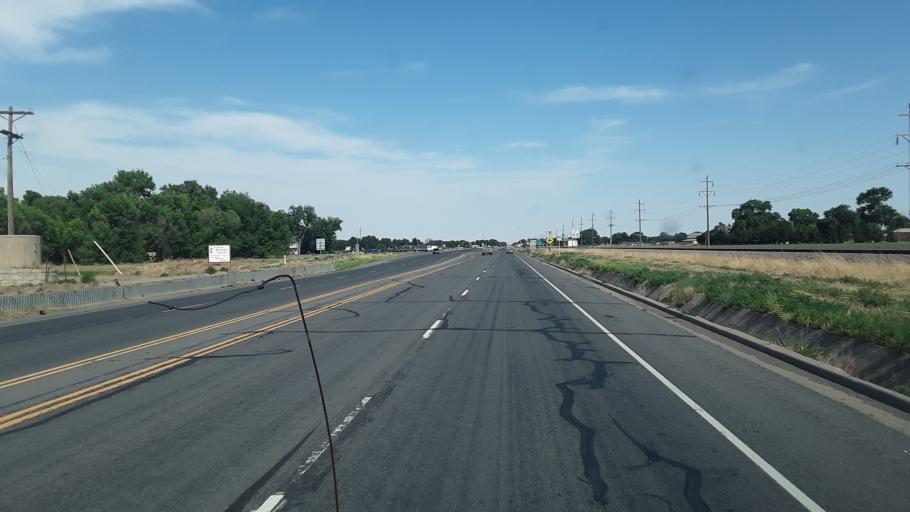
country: US
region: Colorado
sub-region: Otero County
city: Rocky Ford
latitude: 38.0655
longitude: -103.7512
